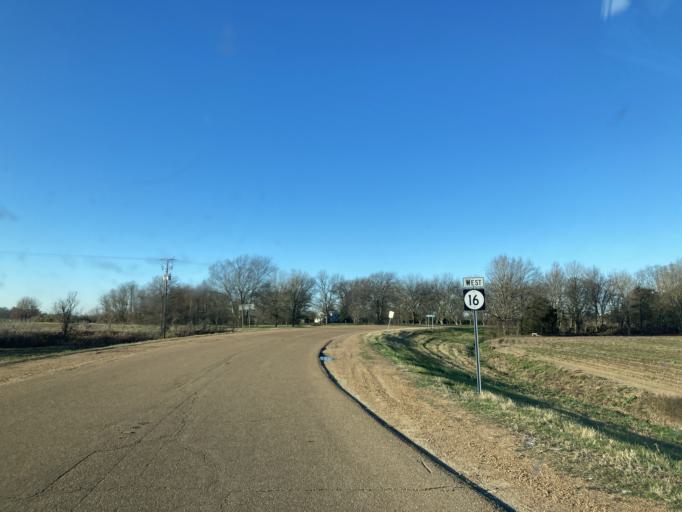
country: US
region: Mississippi
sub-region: Yazoo County
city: Yazoo City
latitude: 32.9285
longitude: -90.5852
